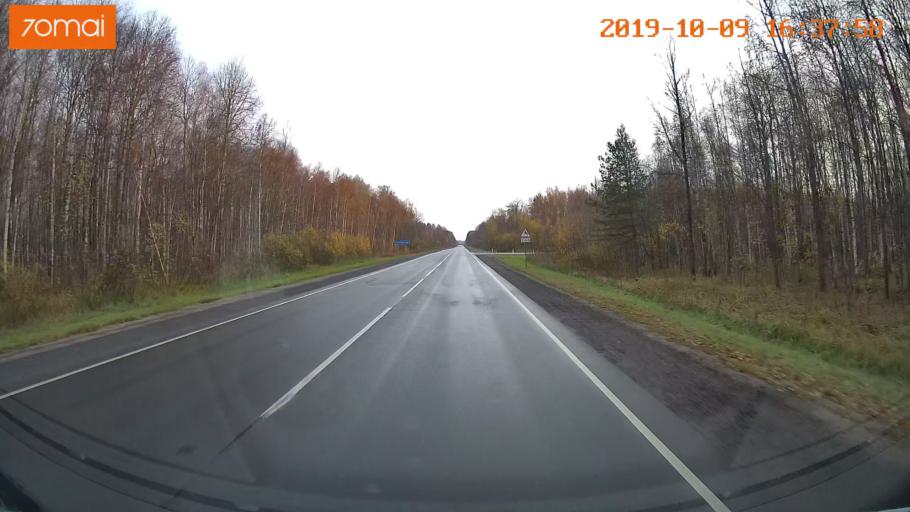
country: RU
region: Kostroma
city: Volgorechensk
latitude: 57.5191
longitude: 41.0312
